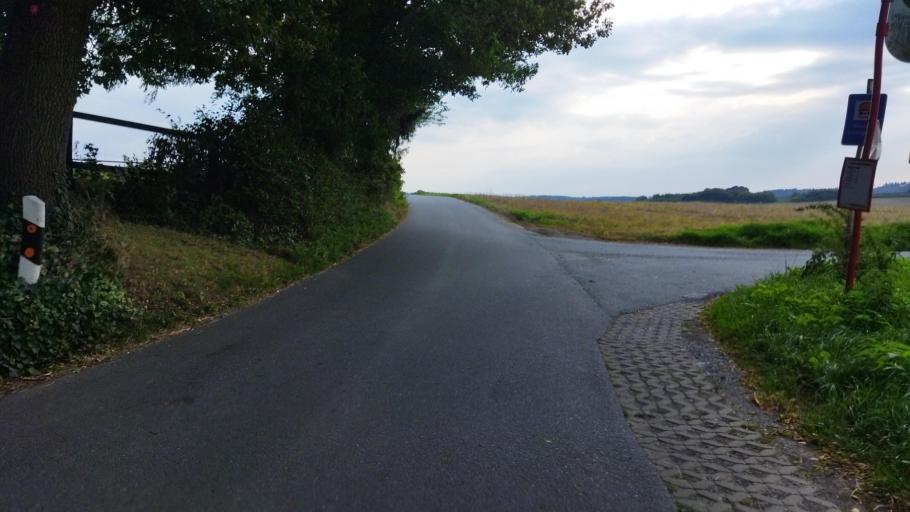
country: DE
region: Lower Saxony
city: Hagen
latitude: 52.1919
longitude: 8.0069
